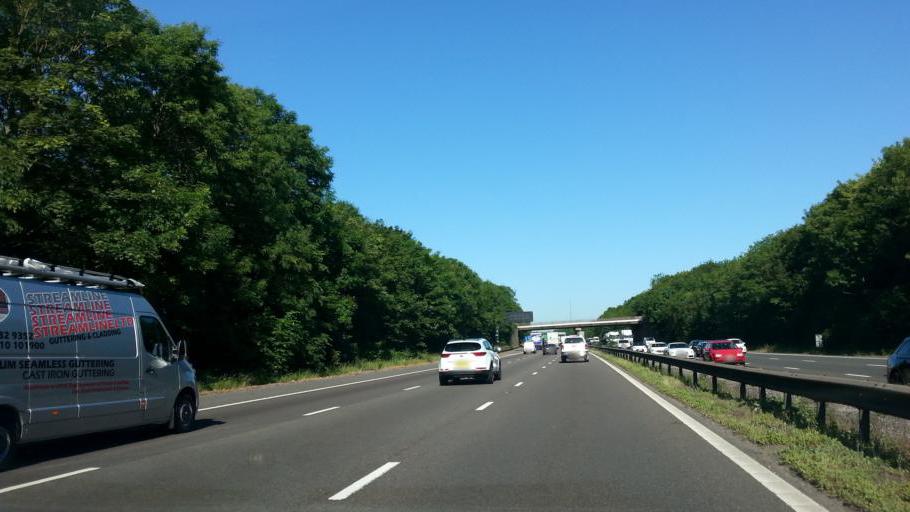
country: GB
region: England
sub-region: Warwickshire
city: Exhall
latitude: 52.4664
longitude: -1.5069
